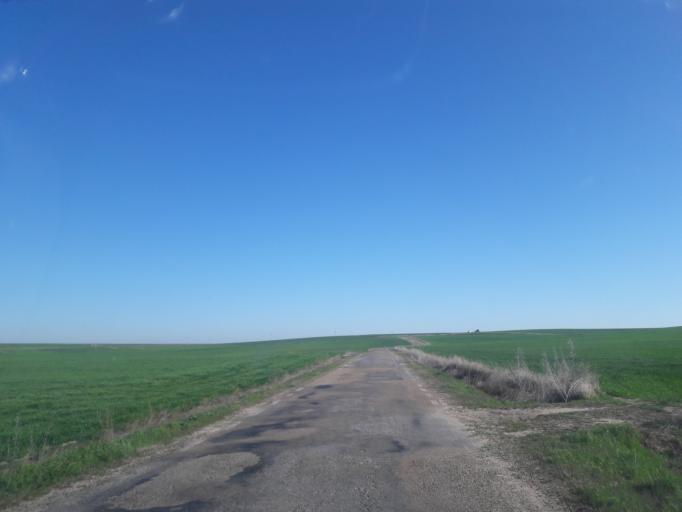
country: ES
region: Castille and Leon
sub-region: Provincia de Salamanca
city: Tordillos
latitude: 40.8717
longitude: -5.3309
